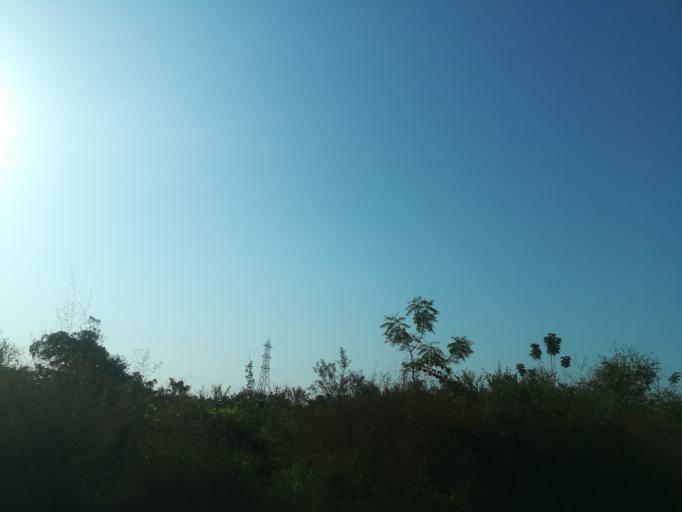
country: NG
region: Ogun
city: Abeokuta
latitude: 7.1962
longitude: 3.2866
